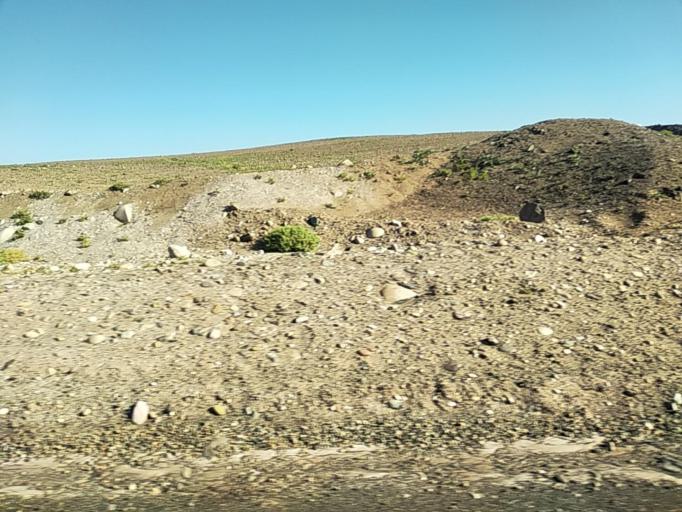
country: CL
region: Atacama
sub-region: Provincia de Copiapo
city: Copiapo
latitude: -27.3282
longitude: -70.7760
